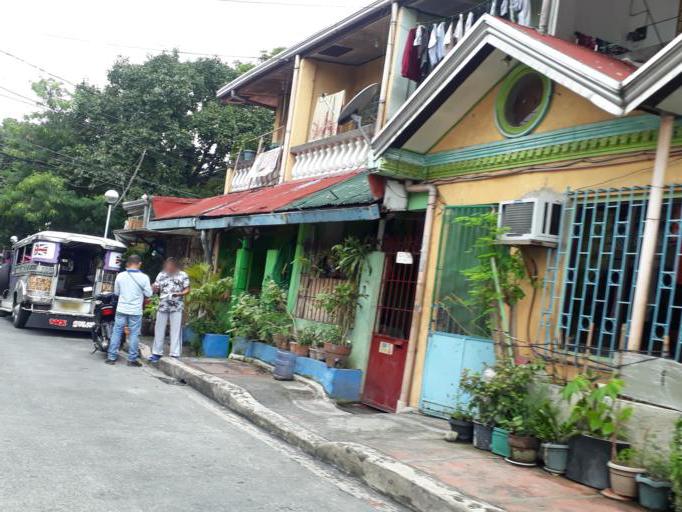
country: PH
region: Calabarzon
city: Bagong Pagasa
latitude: 14.6621
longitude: 121.0345
